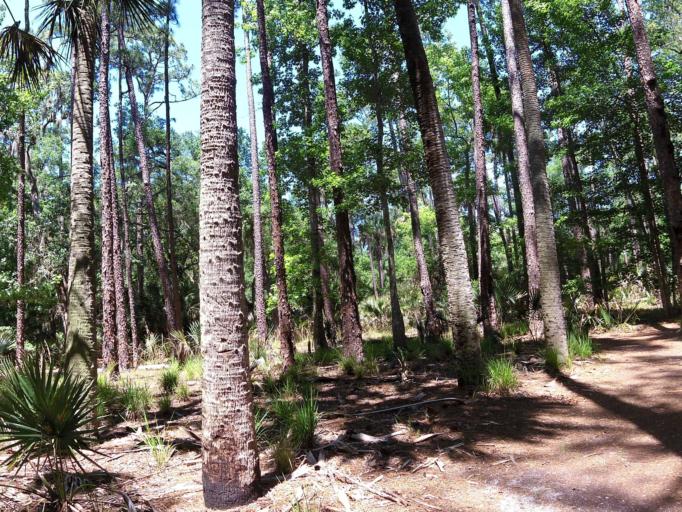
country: US
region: Florida
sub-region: Flagler County
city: Flagler Beach
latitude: 29.4354
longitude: -81.1396
